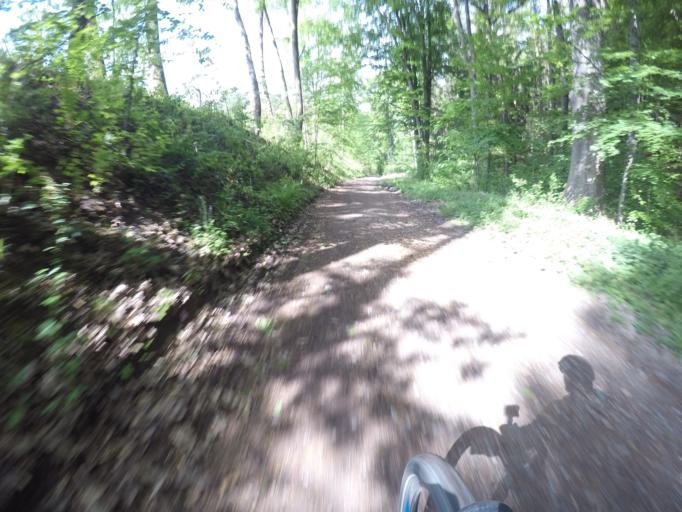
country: DE
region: Baden-Wuerttemberg
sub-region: Tuebingen Region
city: Tuebingen
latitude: 48.5404
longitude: 9.0240
